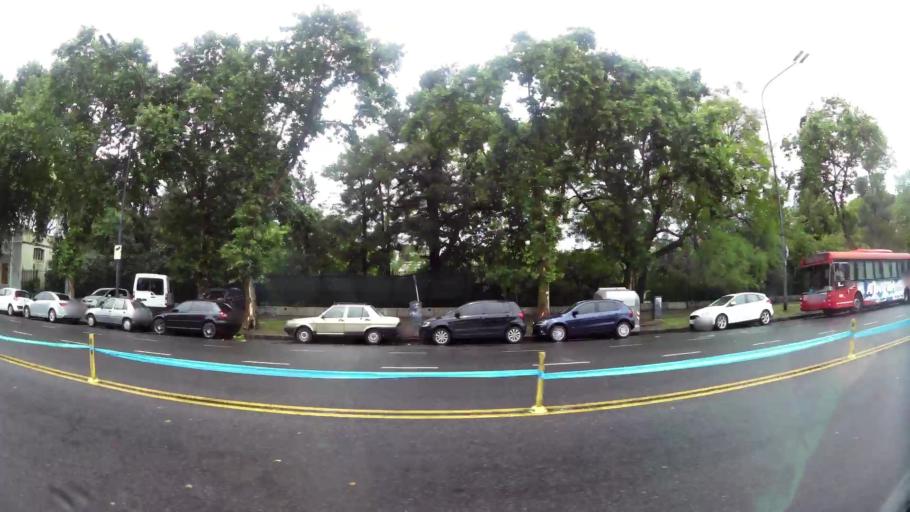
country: AR
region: Buenos Aires F.D.
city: Colegiales
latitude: -34.5800
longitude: -58.4198
